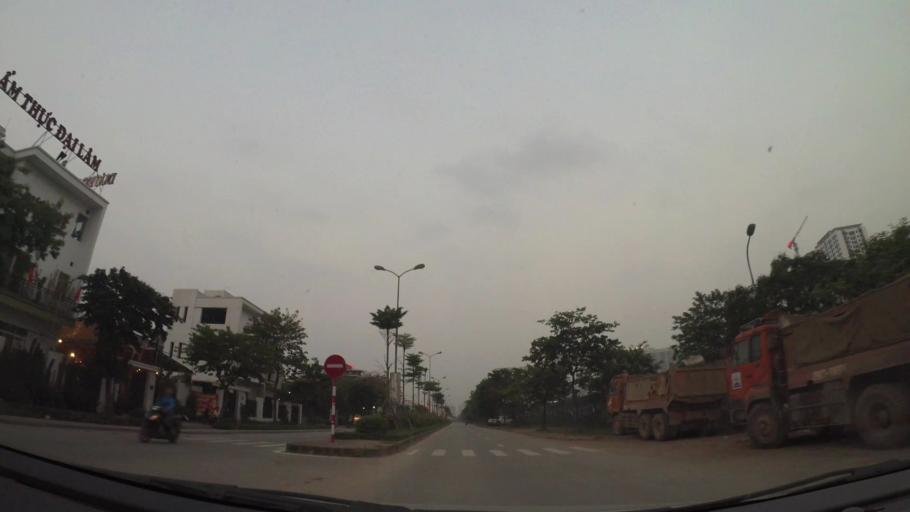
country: VN
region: Ha Noi
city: Tay Ho
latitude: 21.0655
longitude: 105.7912
